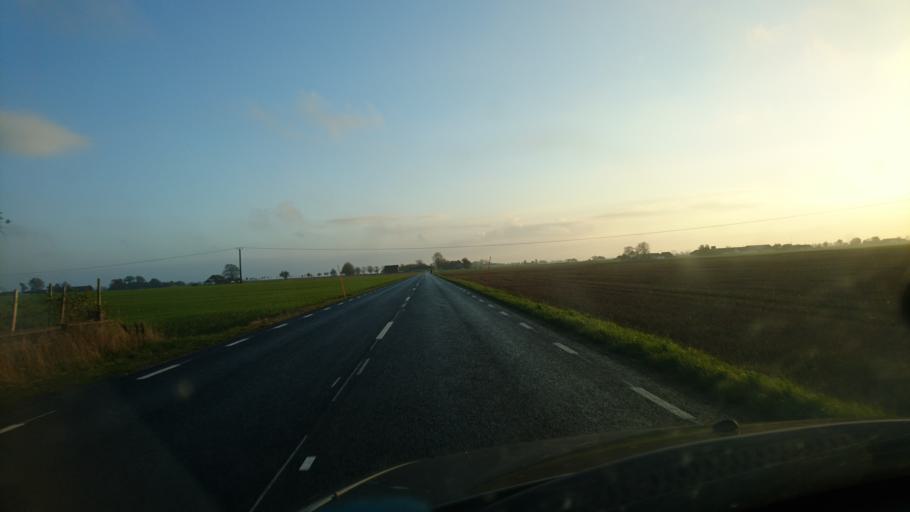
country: SE
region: Skane
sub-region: Simrishamns Kommun
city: Simrishamn
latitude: 55.4491
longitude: 14.1772
